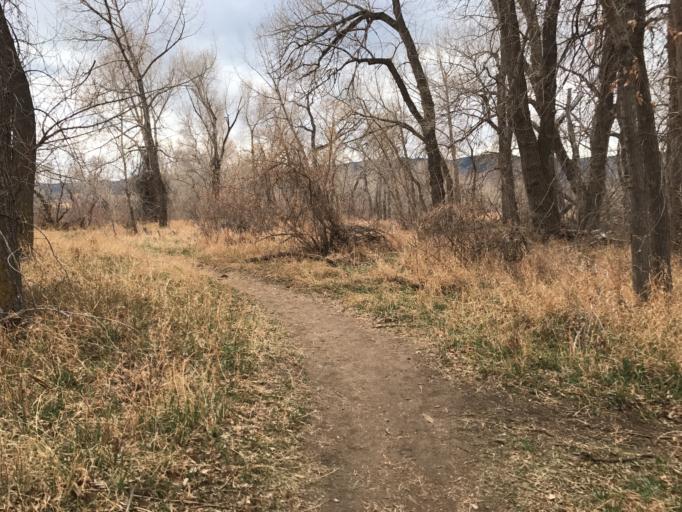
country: US
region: Colorado
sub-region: Douglas County
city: Roxborough Park
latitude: 39.5017
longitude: -105.0852
